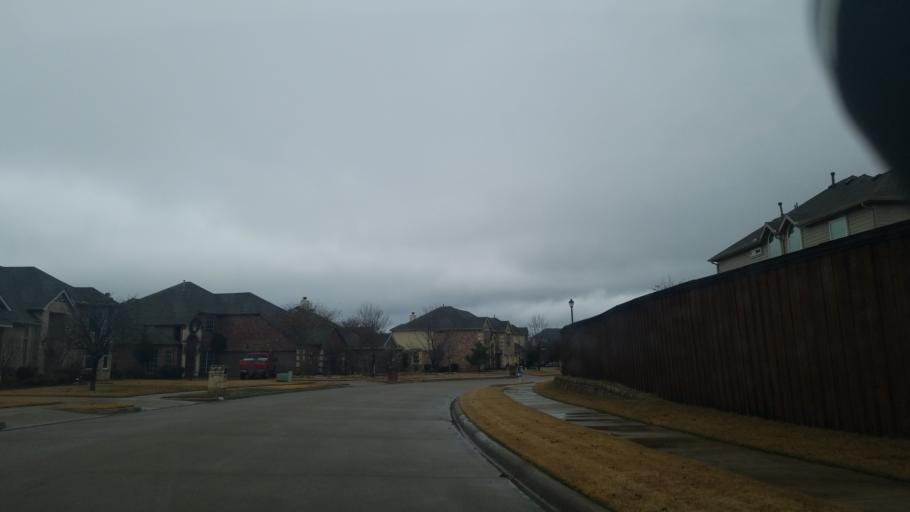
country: US
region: Texas
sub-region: Denton County
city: Corinth
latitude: 33.1388
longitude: -97.0916
